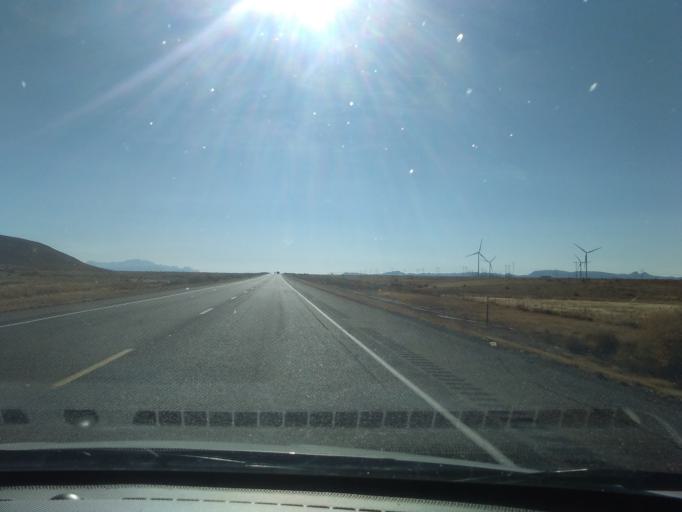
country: US
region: New Mexico
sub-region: Dona Ana County
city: Hatch
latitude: 32.5505
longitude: -107.4770
